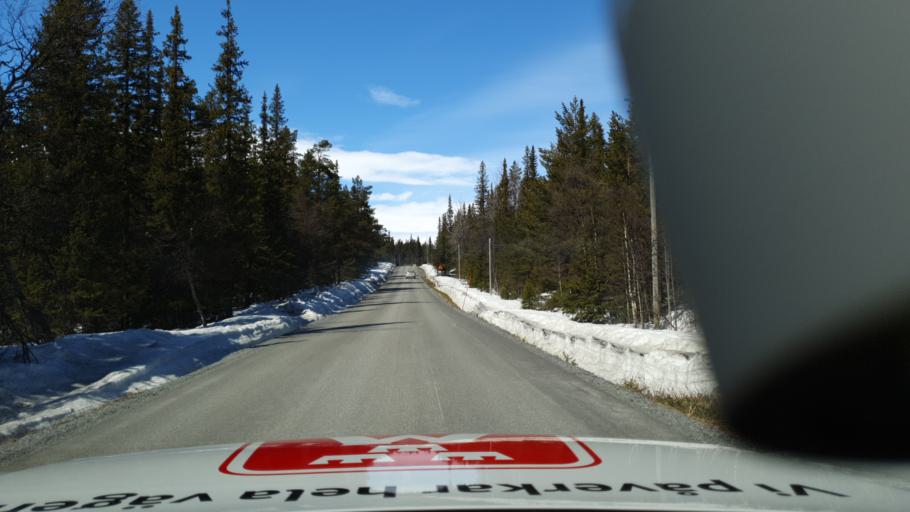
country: SE
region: Jaemtland
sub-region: Are Kommun
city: Are
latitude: 62.8647
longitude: 12.7610
